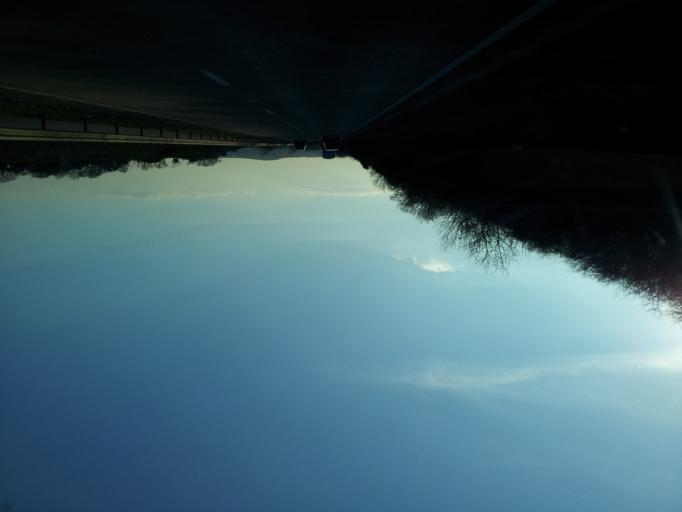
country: GB
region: England
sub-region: Devon
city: Okehampton
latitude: 50.7326
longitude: -3.8862
